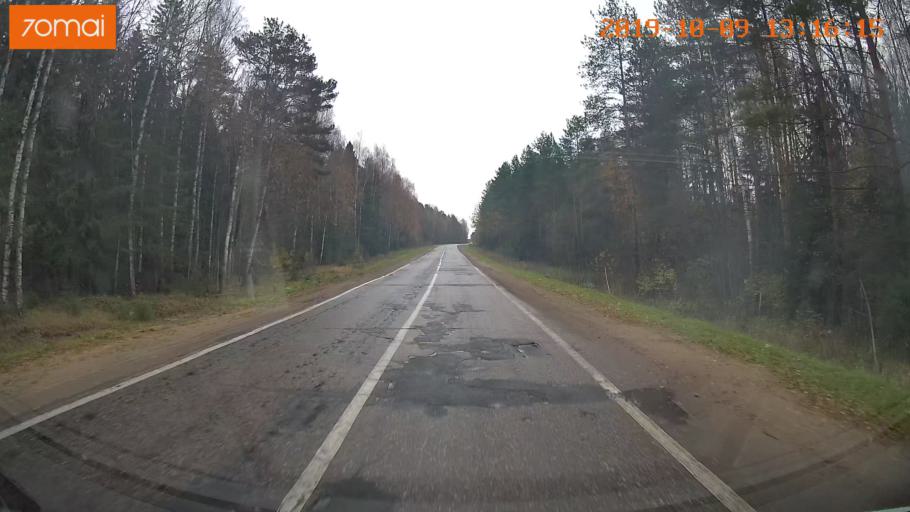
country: RU
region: Jaroslavl
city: Lyubim
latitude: 58.3625
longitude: 40.7632
